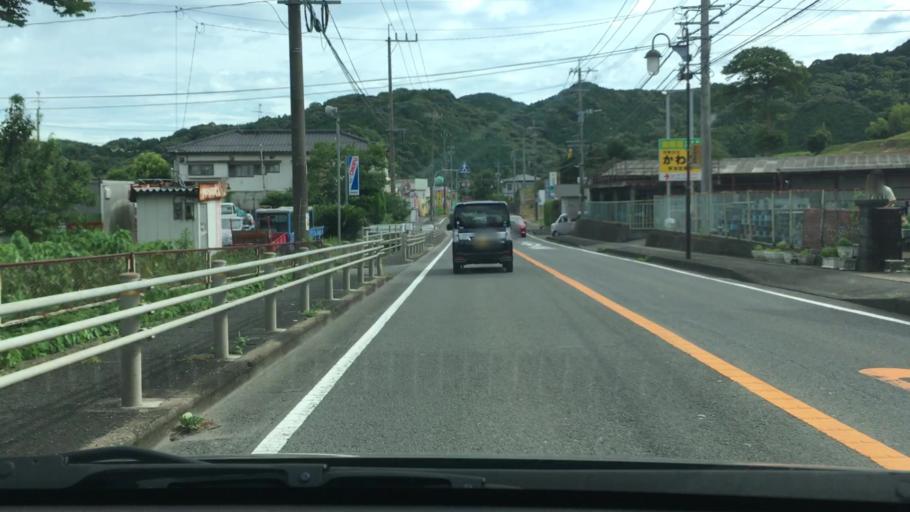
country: JP
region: Nagasaki
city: Togitsu
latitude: 32.8975
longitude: 129.7808
